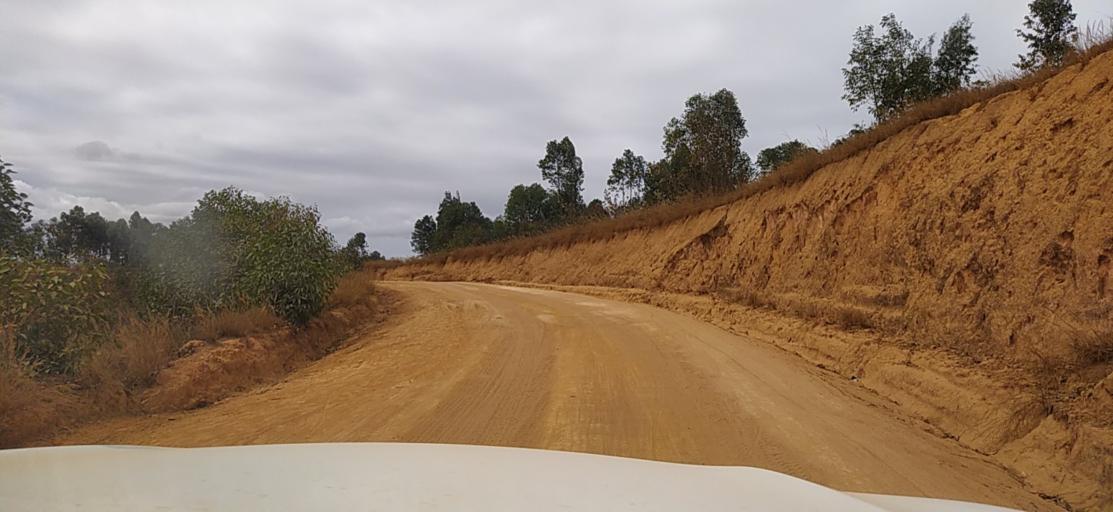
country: MG
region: Alaotra Mangoro
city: Ambatondrazaka
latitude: -17.9977
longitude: 48.2672
